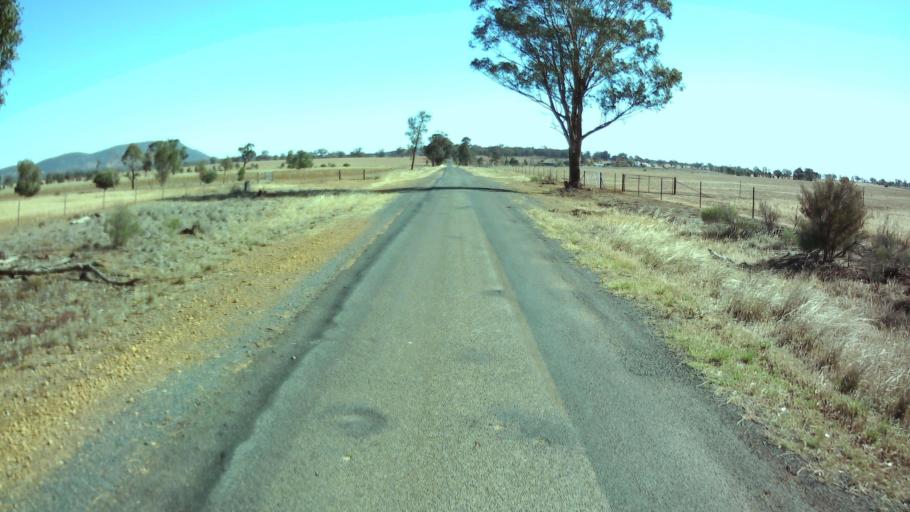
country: AU
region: New South Wales
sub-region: Weddin
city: Grenfell
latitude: -33.7996
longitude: 147.9560
